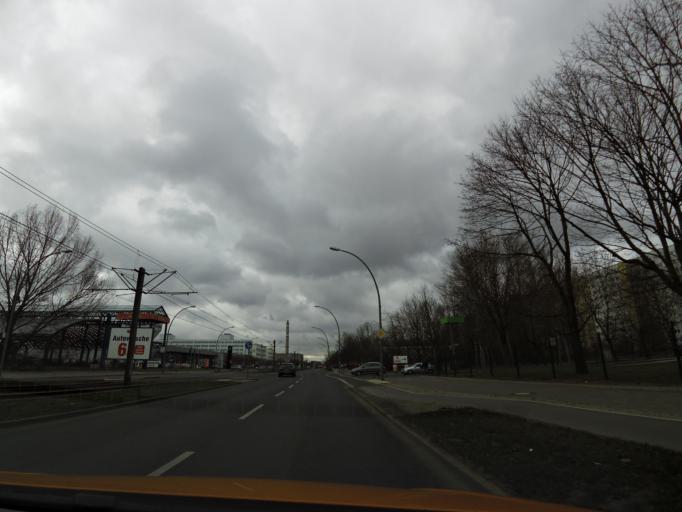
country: DE
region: Berlin
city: Alt-Hohenschoenhausen
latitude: 52.5319
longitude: 13.5189
